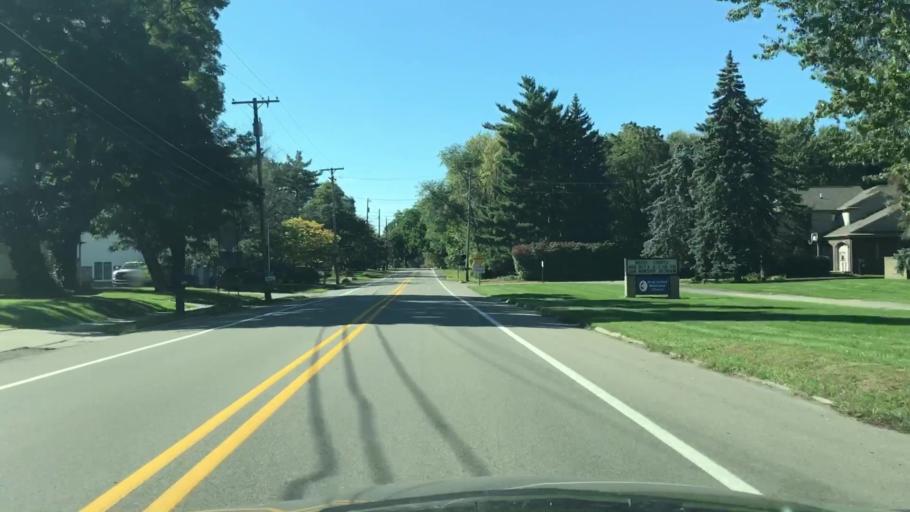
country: US
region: Michigan
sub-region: Macomb County
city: Center Line
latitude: 42.5277
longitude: -83.0567
